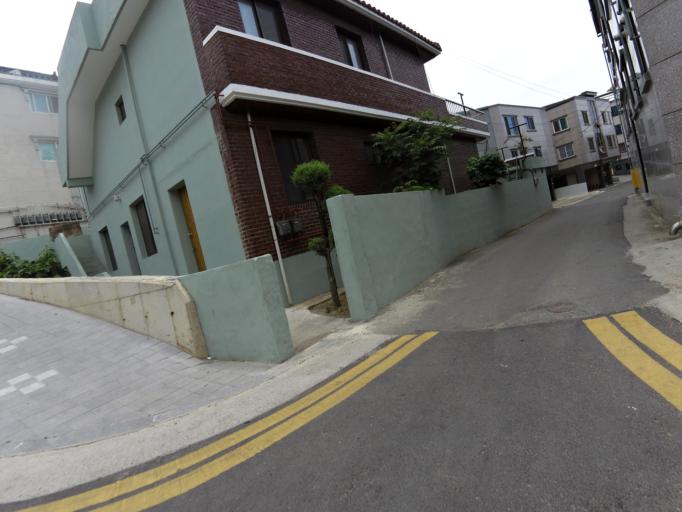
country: KR
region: Gyeongsangbuk-do
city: Gyeongsan-si
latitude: 35.8393
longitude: 128.7511
